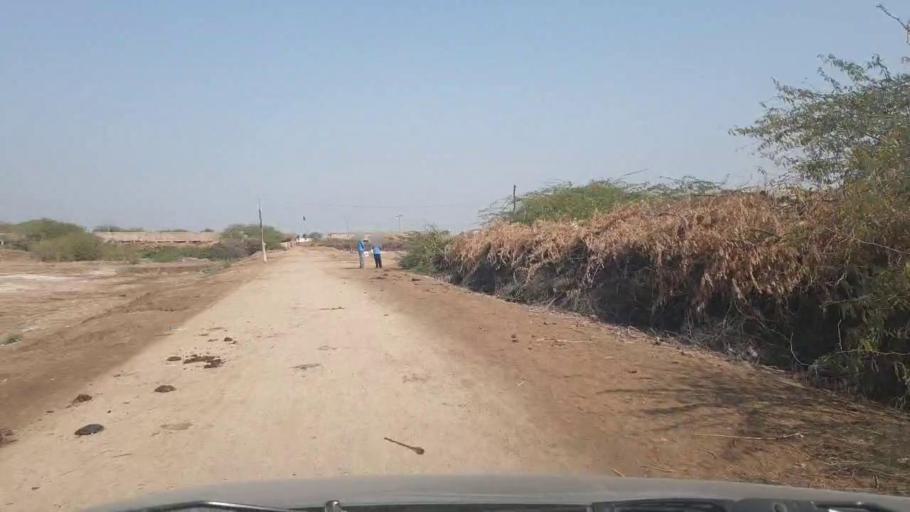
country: PK
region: Sindh
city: Mirwah Gorchani
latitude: 25.2781
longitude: 69.1380
